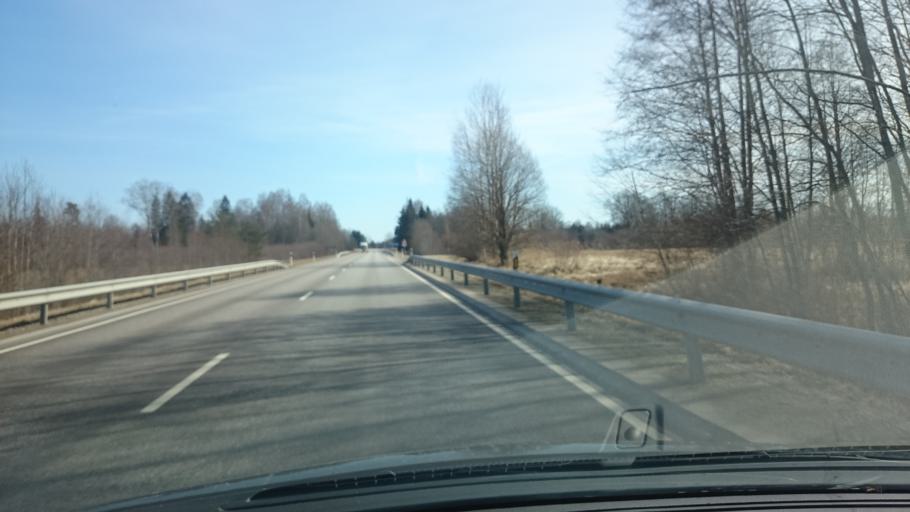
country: EE
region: Paernumaa
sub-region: Vaendra vald (alev)
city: Vandra
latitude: 58.6687
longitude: 25.1395
